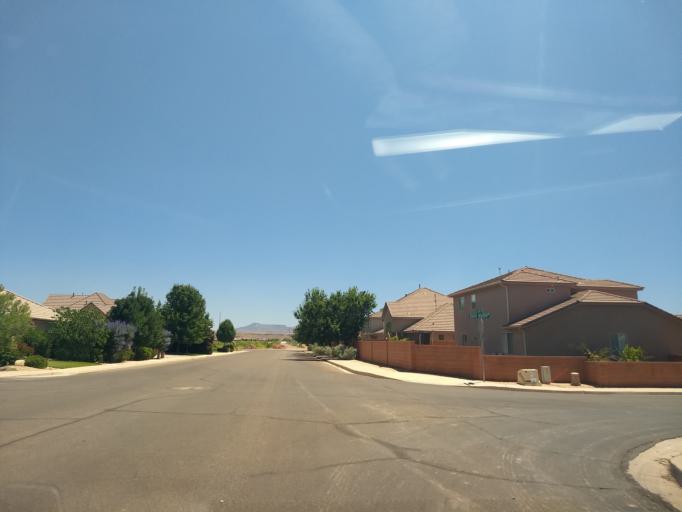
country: US
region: Utah
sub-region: Washington County
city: Washington
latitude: 37.0975
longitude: -113.5136
